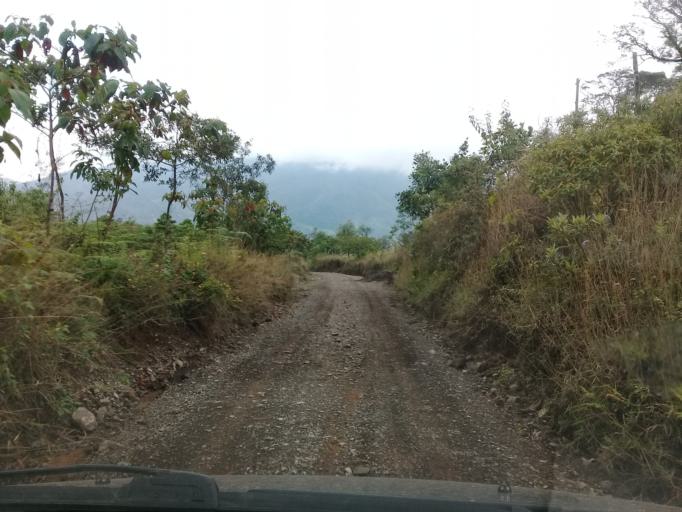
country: CO
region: Cundinamarca
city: Viani
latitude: 4.8431
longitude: -74.5531
